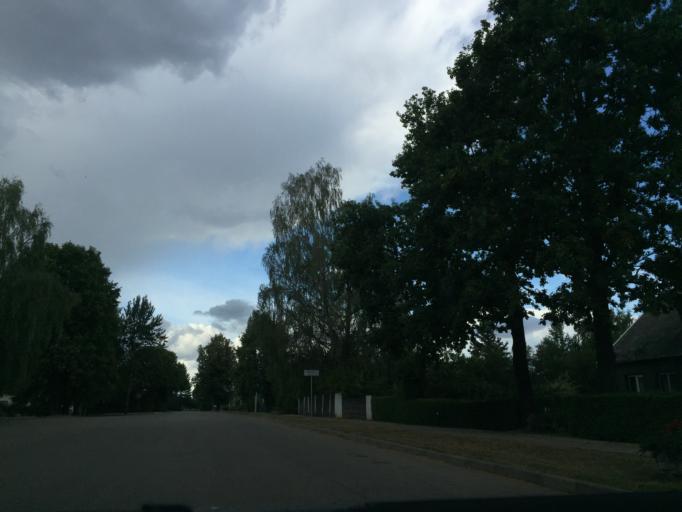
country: LV
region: Tervete
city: Zelmeni
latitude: 56.3079
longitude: 23.3927
